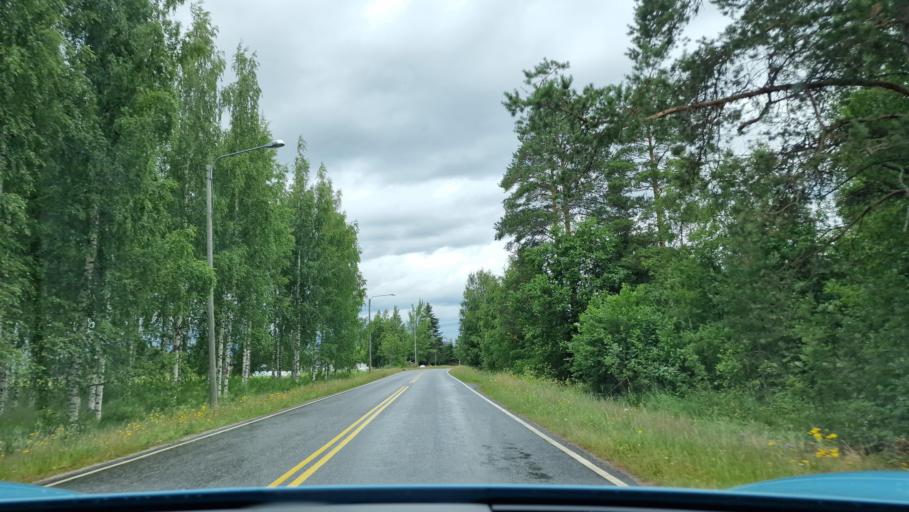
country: FI
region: Southern Ostrobothnia
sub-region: Jaerviseutu
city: Soini
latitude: 62.6985
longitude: 24.4535
